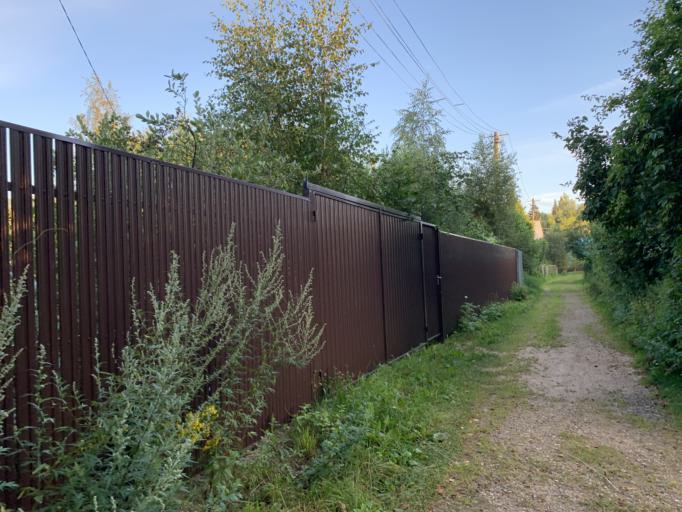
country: RU
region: Moskovskaya
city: Podosinki
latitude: 56.1767
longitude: 37.5789
